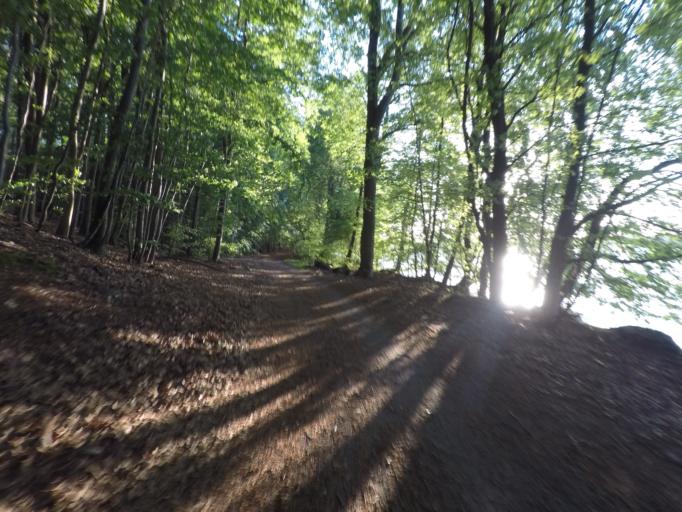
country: DE
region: Brandenburg
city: Joachimsthal
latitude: 52.9044
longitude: 13.6865
